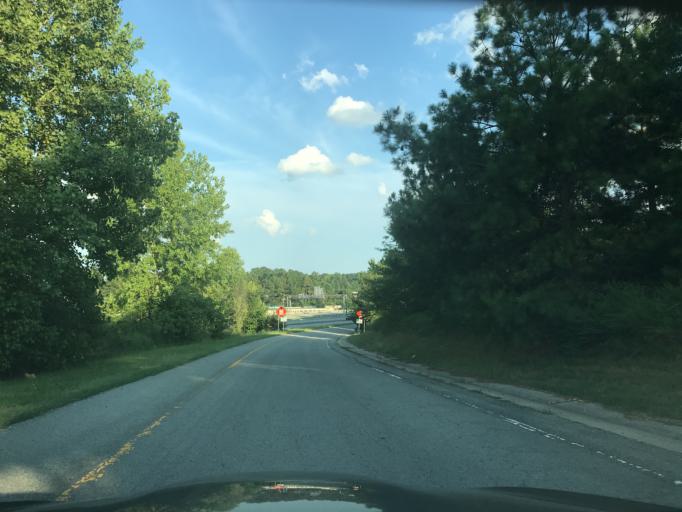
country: US
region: North Carolina
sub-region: Durham County
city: Durham
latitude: 36.0040
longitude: -78.8649
